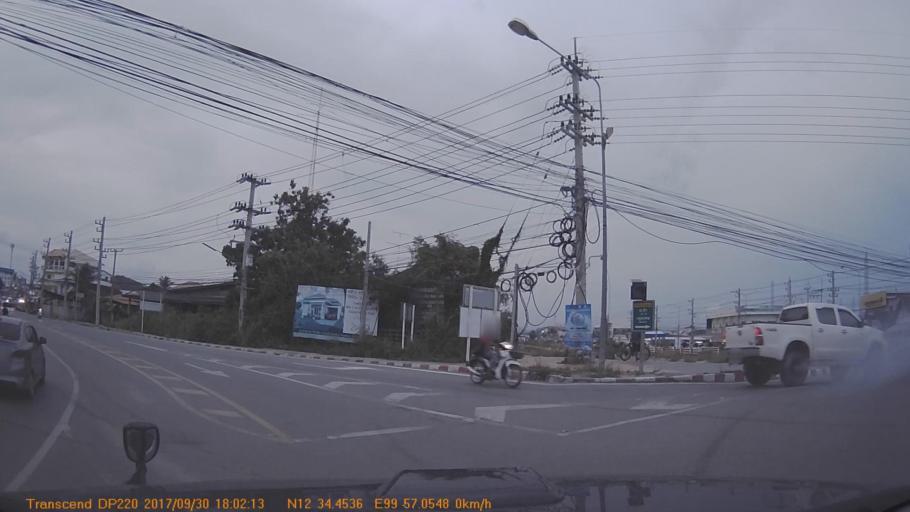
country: TH
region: Prachuap Khiri Khan
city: Hua Hin
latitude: 12.5748
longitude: 99.9507
